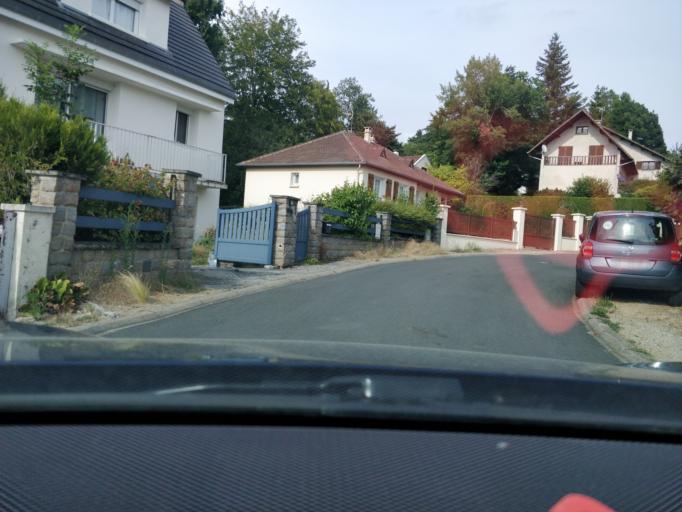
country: FR
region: Ile-de-France
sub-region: Departement de l'Essonne
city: Briis-sous-Forges
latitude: 48.6314
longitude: 2.1212
